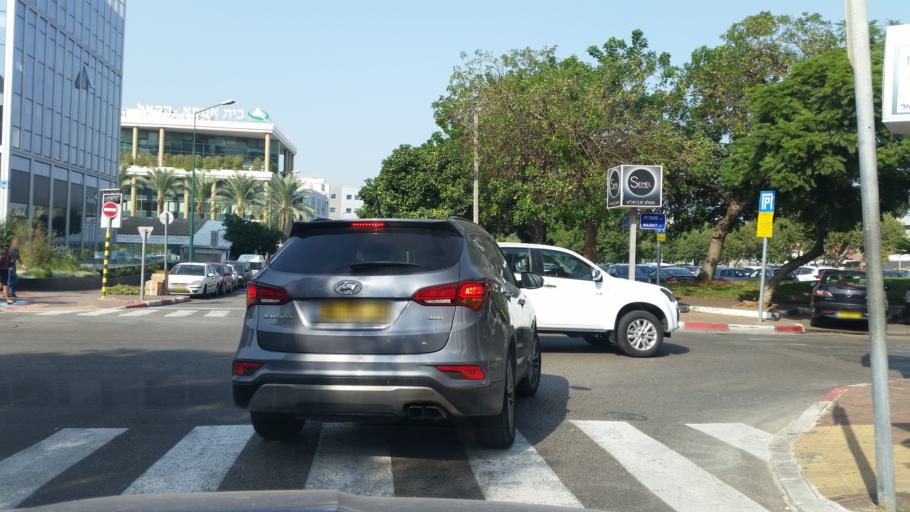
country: IL
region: Tel Aviv
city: Herzliya Pituah
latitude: 32.1631
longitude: 34.8103
